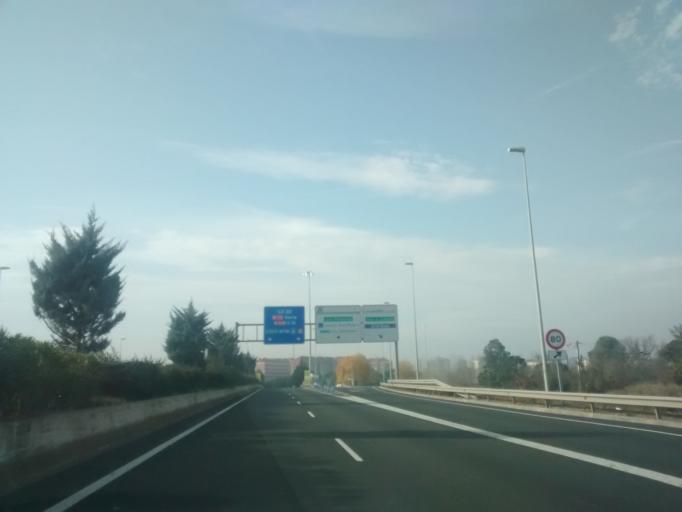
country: ES
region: La Rioja
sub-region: Provincia de La Rioja
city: Villamediana de Iregua
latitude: 42.4563
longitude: -2.4210
